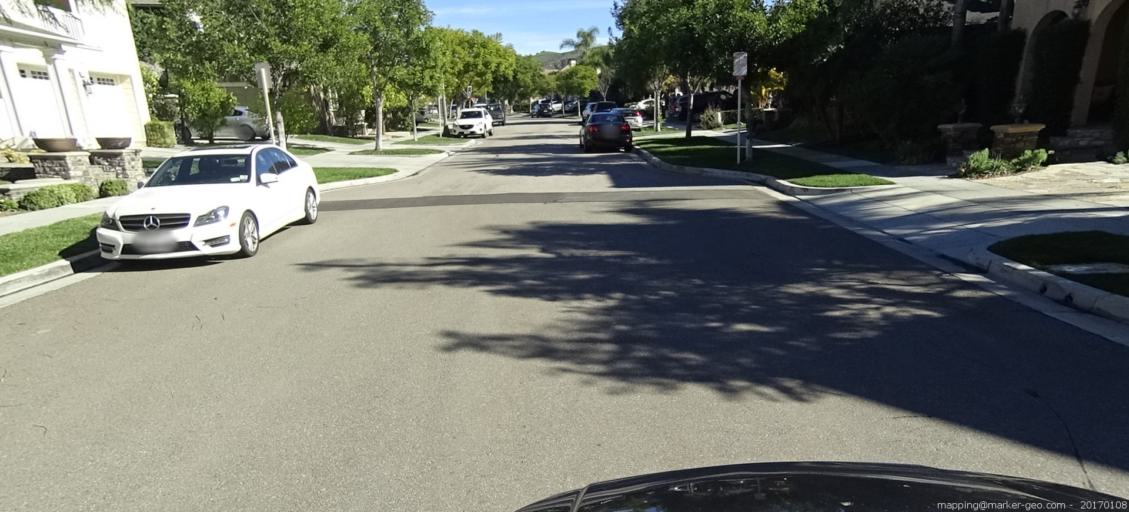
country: US
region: California
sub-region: Orange County
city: Ladera Ranch
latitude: 33.5574
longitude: -117.6398
